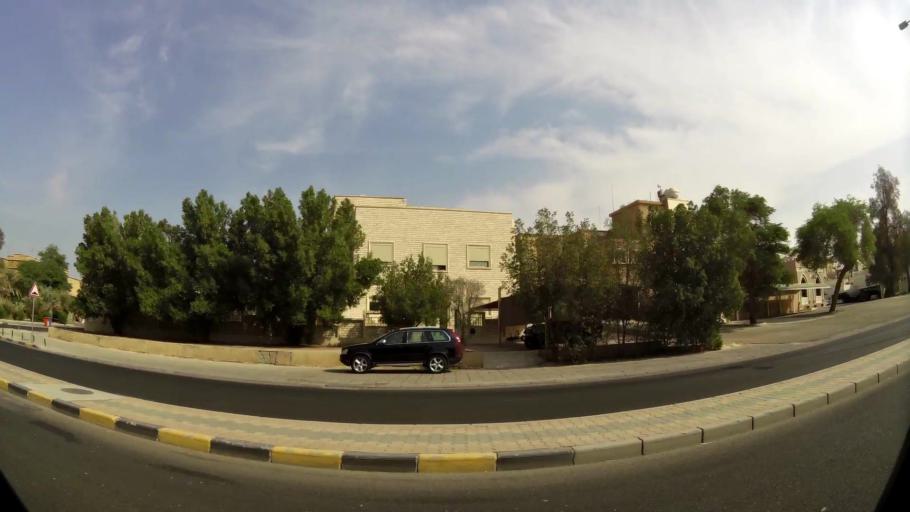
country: KW
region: Al Asimah
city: Ash Shamiyah
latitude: 29.3473
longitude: 47.9678
